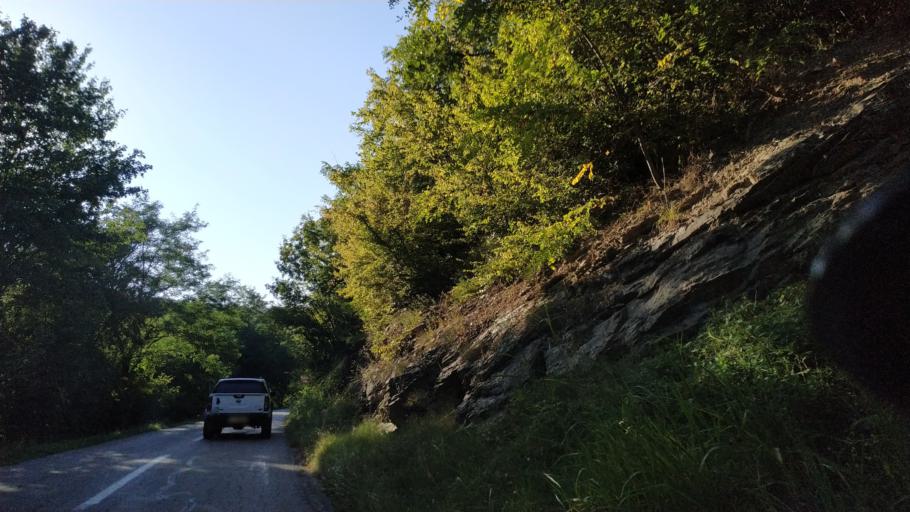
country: RS
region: Central Serbia
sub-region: Rasinski Okrug
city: Krusevac
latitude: 43.4692
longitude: 21.3589
